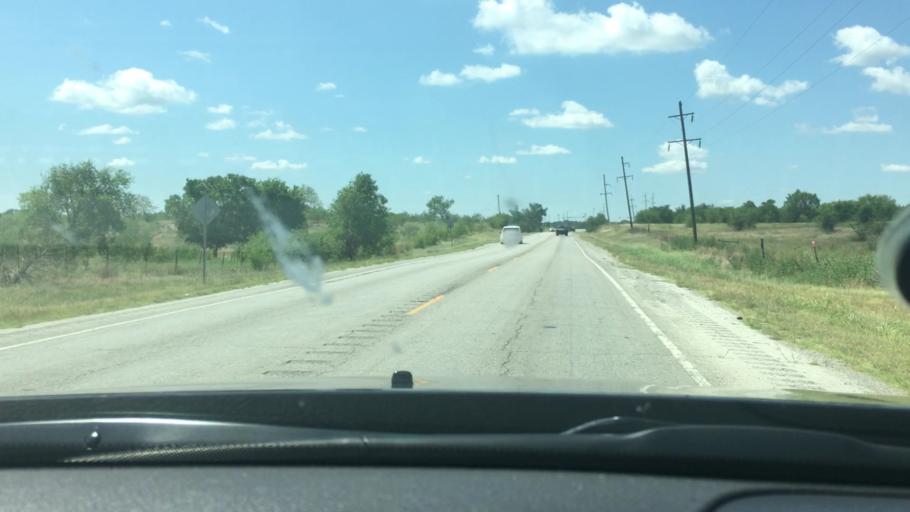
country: US
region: Oklahoma
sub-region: Carter County
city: Ardmore
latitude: 34.0755
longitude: -97.1429
